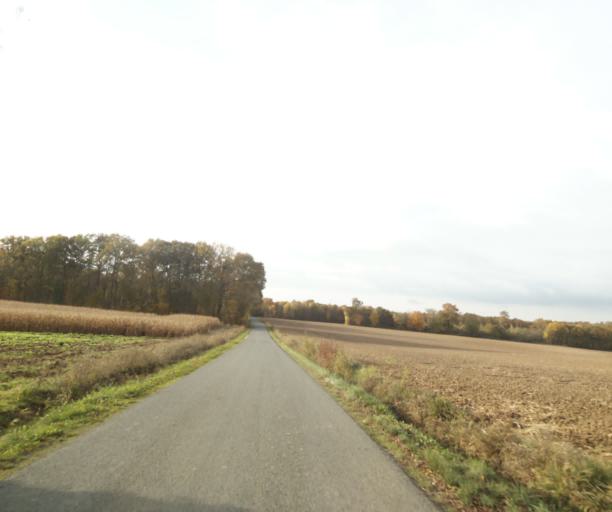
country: FR
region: Poitou-Charentes
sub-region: Departement de la Charente-Maritime
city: Nieul-les-Saintes
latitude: 45.7774
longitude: -0.7333
